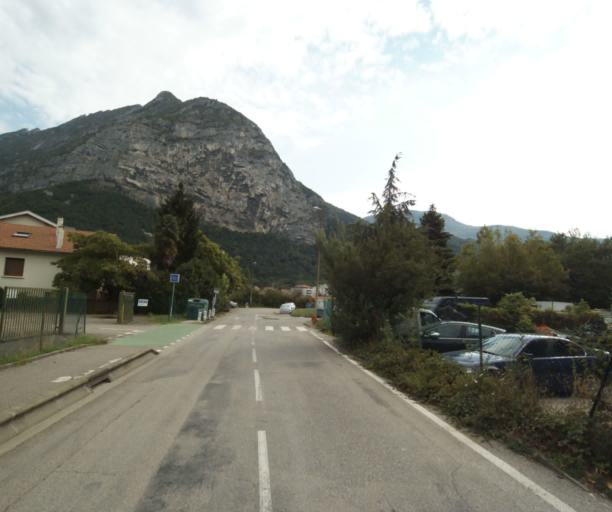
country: FR
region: Rhone-Alpes
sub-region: Departement de l'Isere
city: Fontaine
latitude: 45.2127
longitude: 5.6917
